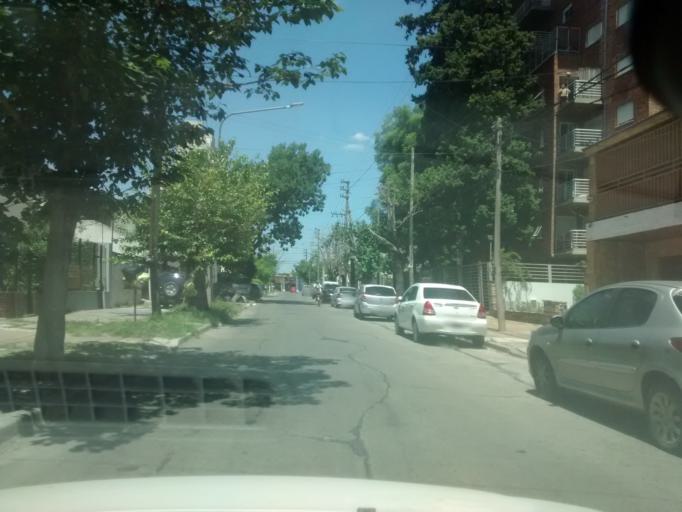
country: AR
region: Buenos Aires
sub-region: Partido de Moron
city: Moron
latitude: -34.6585
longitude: -58.6164
